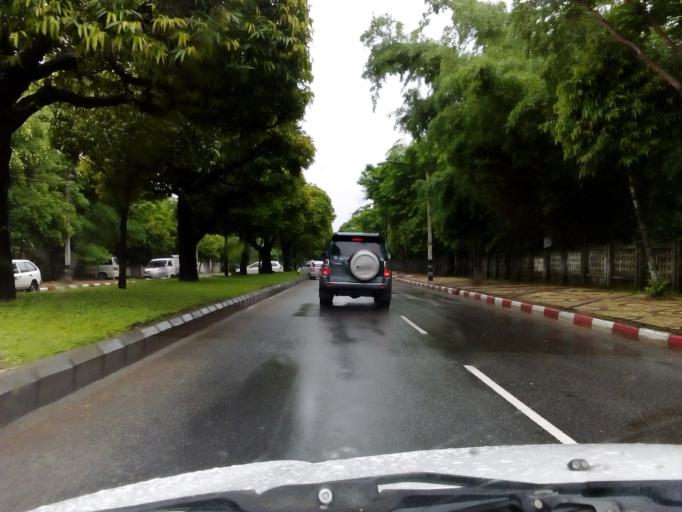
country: MM
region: Yangon
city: Yangon
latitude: 16.7876
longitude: 96.1499
